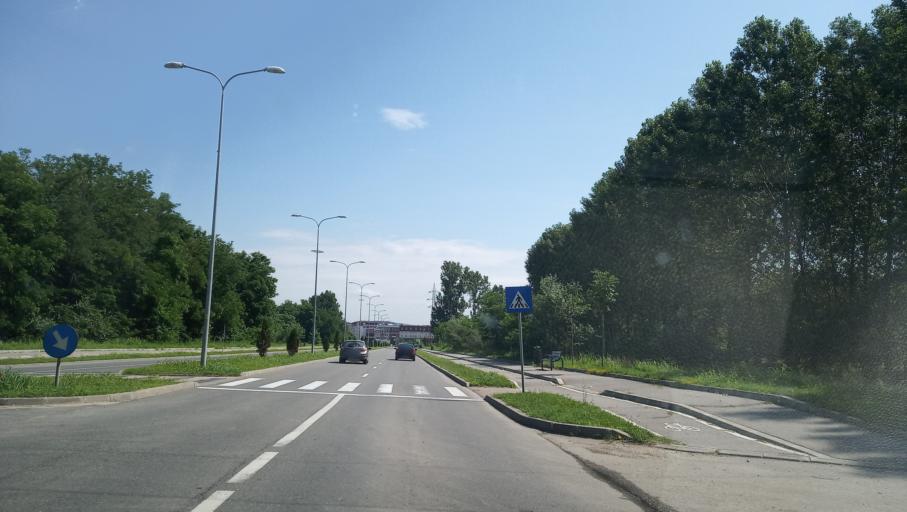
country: RO
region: Valcea
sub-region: Municipiul Ramnicu Valcea
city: Ramnicu Valcea
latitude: 45.0779
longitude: 24.3628
